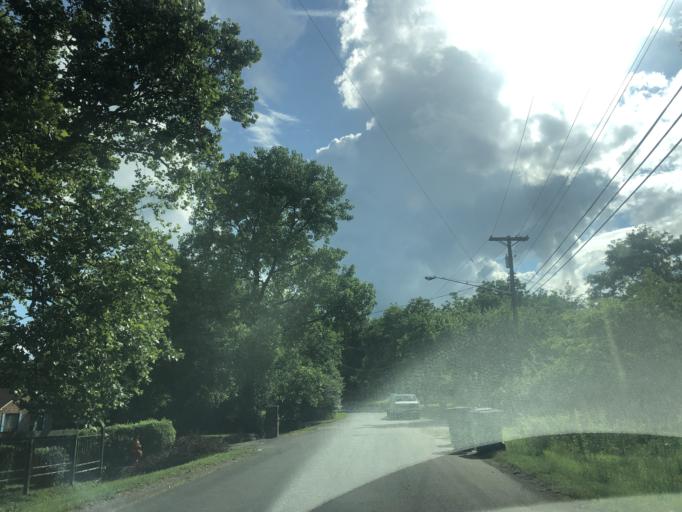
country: US
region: Tennessee
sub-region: Davidson County
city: Nashville
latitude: 36.2117
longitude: -86.8546
